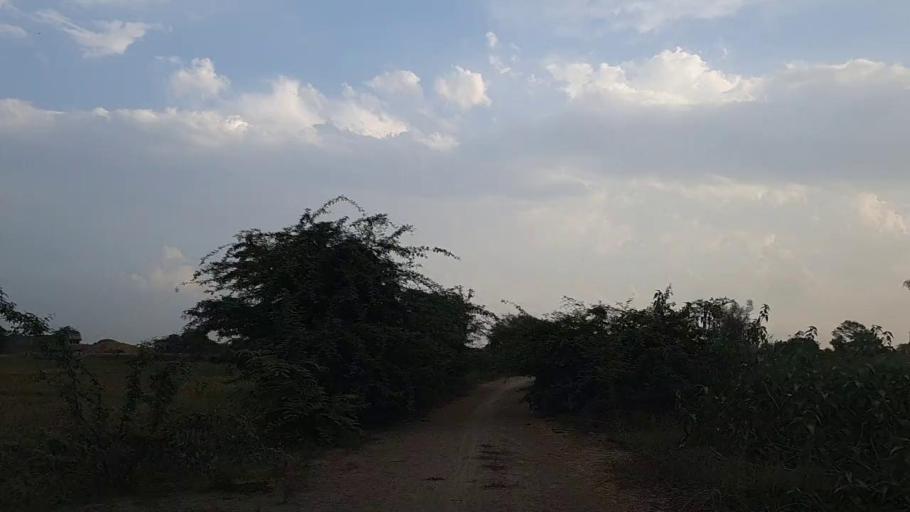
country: PK
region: Sindh
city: Daro Mehar
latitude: 24.7684
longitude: 68.1429
